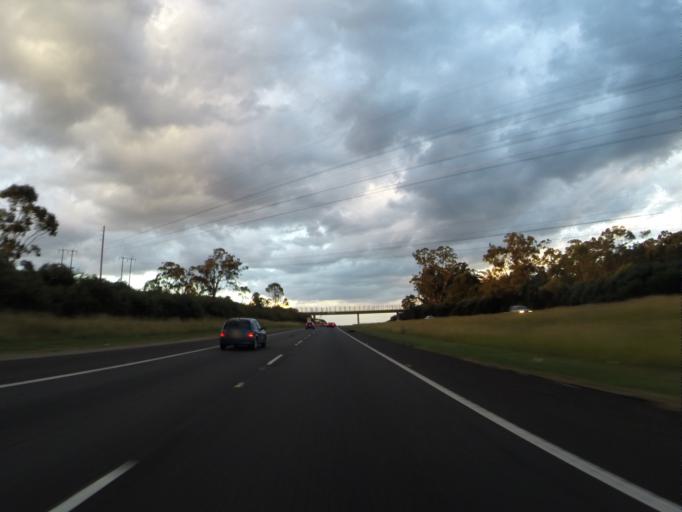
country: AU
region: New South Wales
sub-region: Campbelltown Municipality
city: Glen Alpine
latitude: -34.0896
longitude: 150.7674
